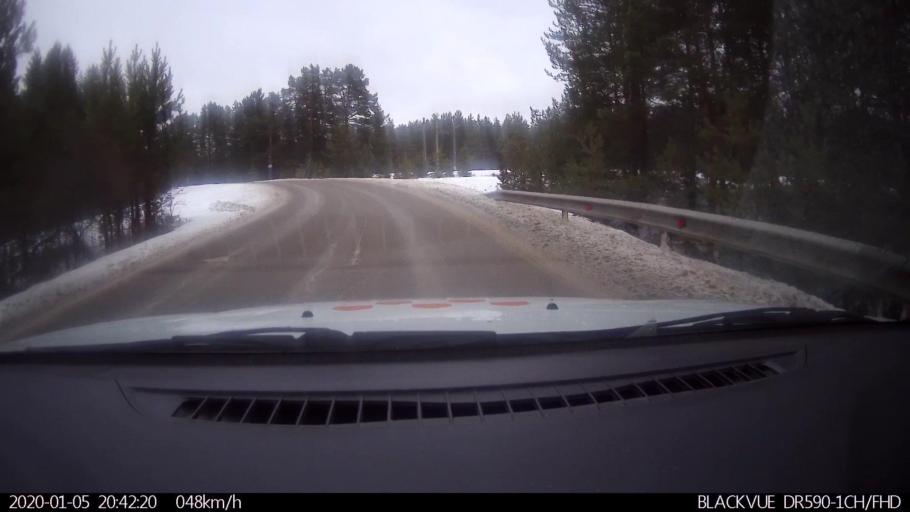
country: RU
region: Nizjnij Novgorod
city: Lukino
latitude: 56.3969
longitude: 43.7299
